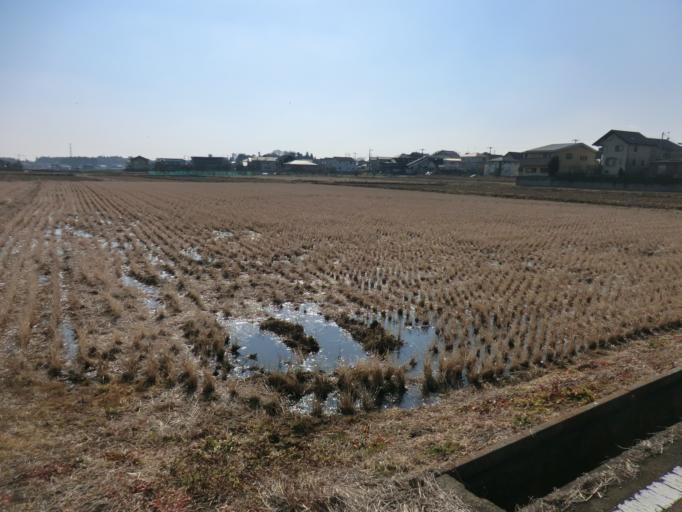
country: JP
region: Ibaraki
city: Naka
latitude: 36.0806
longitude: 140.1293
